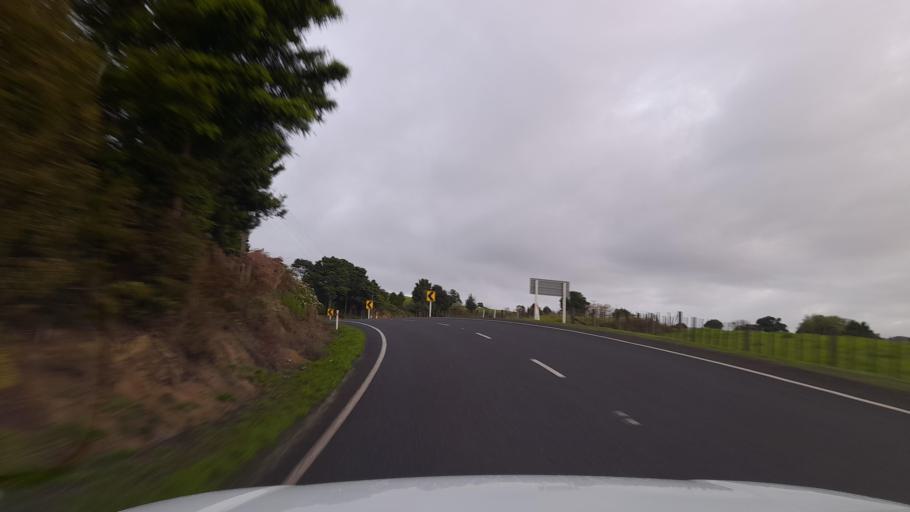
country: NZ
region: Northland
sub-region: Whangarei
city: Maungatapere
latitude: -35.7322
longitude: 174.0474
